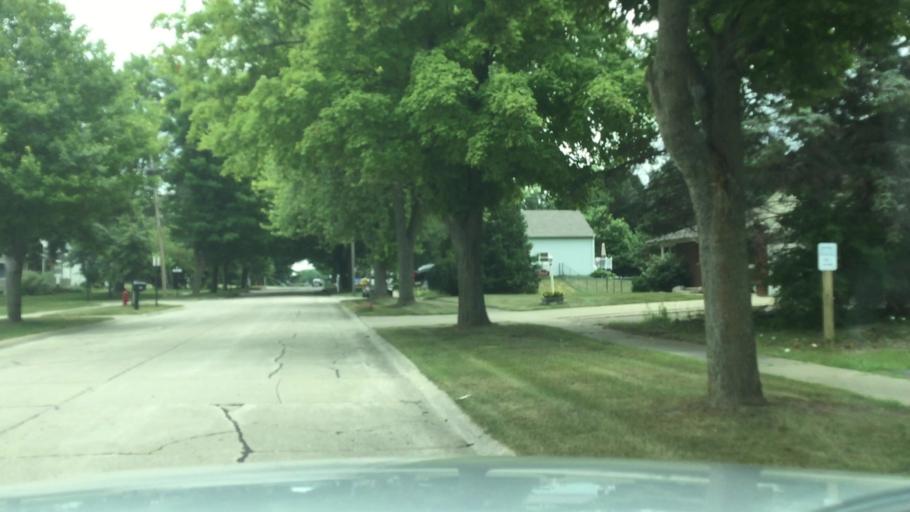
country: US
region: Michigan
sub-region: Saginaw County
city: Frankenmuth
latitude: 43.3213
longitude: -83.7373
